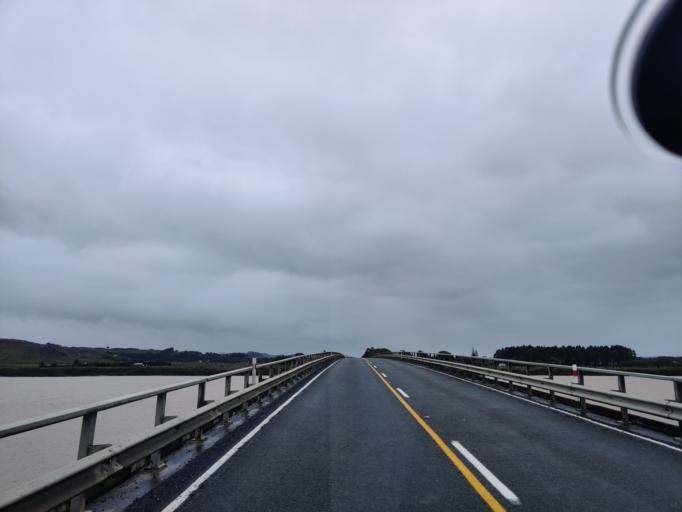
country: NZ
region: Northland
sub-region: Kaipara District
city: Dargaville
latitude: -35.9382
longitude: 173.8833
